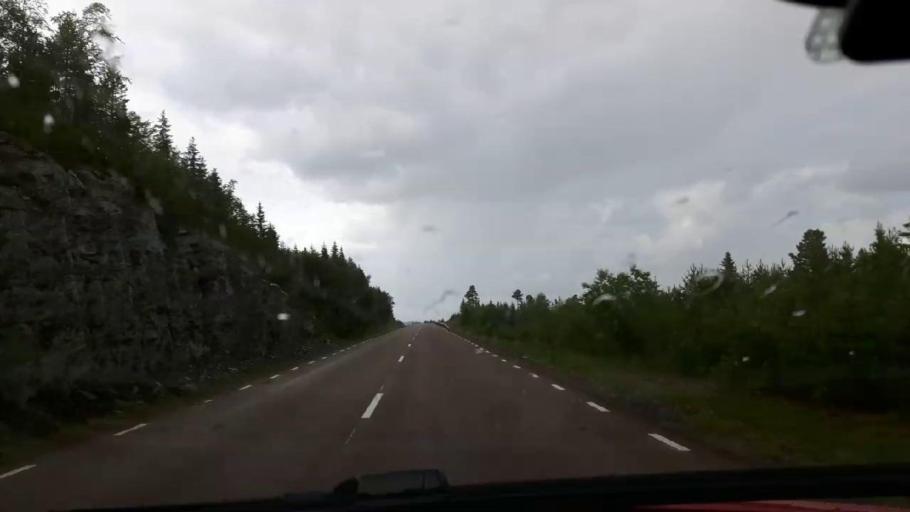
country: SE
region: Jaemtland
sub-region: Krokoms Kommun
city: Krokom
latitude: 63.8857
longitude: 14.2814
